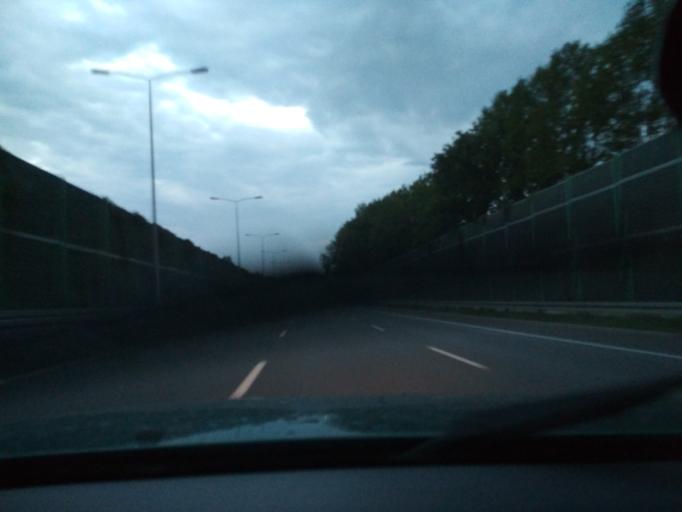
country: PL
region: Silesian Voivodeship
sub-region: Powiat gliwicki
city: Przyszowice
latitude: 50.2822
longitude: 18.7389
